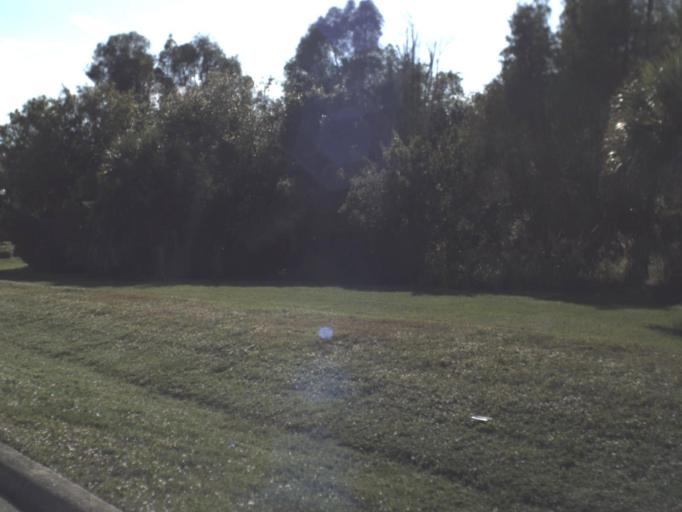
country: US
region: Florida
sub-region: Brevard County
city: South Patrick Shores
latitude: 28.1553
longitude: -80.6720
